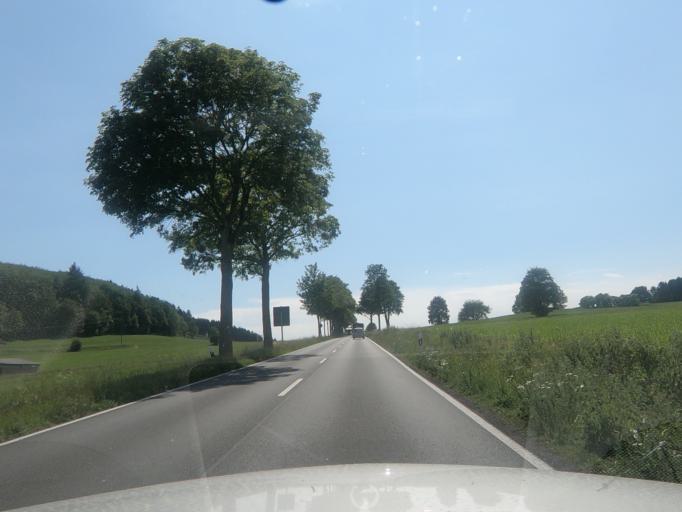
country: DE
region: North Rhine-Westphalia
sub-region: Regierungsbezirk Arnsberg
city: Sundern
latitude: 51.2936
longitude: 7.9795
